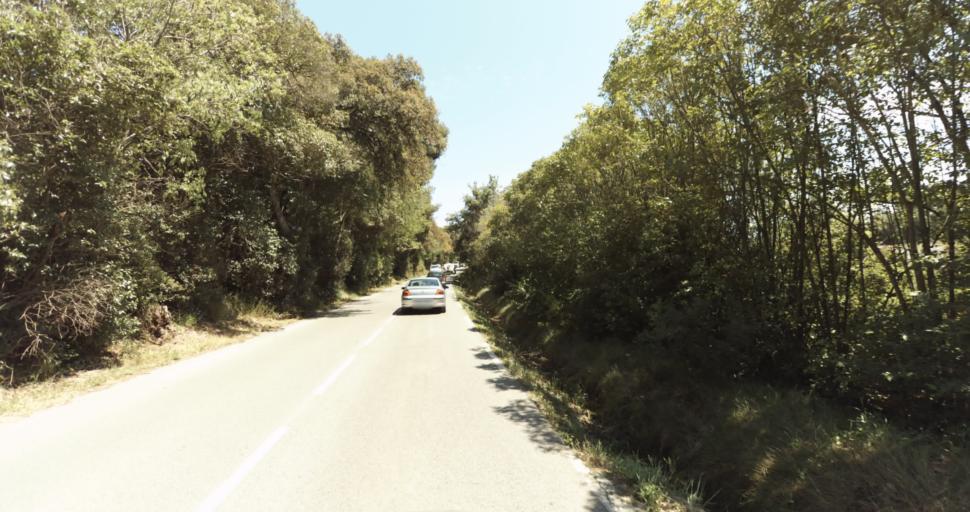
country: FR
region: Provence-Alpes-Cote d'Azur
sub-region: Departement du Var
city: Hyeres
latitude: 43.1520
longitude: 6.1420
